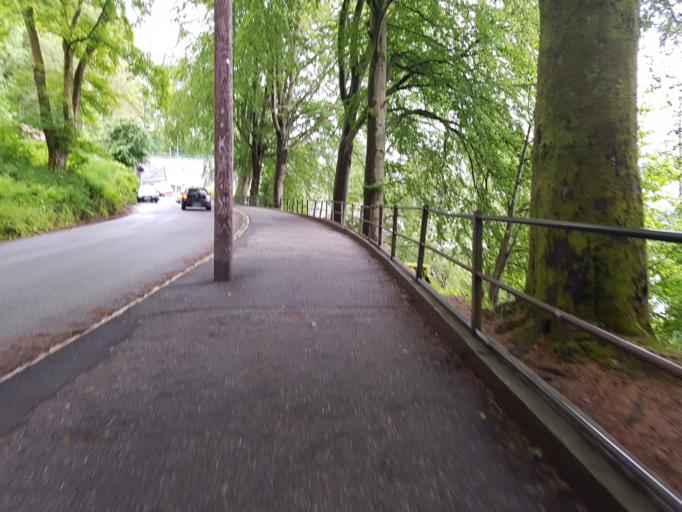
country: NO
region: Hordaland
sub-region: Bergen
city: Bergen
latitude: 60.3966
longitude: 5.3332
